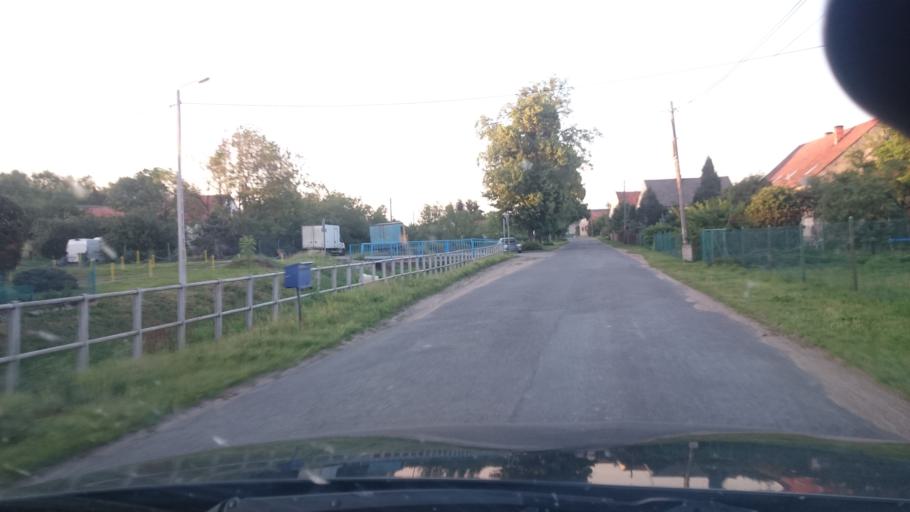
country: PL
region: Lower Silesian Voivodeship
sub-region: Powiat zabkowicki
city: Kamieniec Zabkowicki
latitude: 50.4923
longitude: 16.8274
